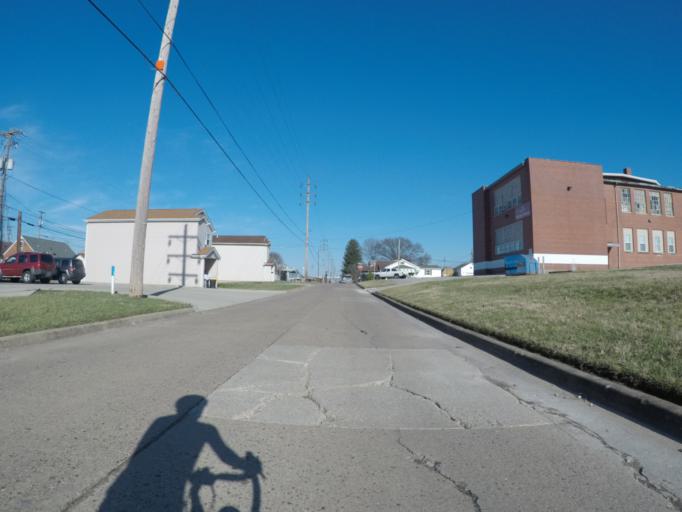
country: US
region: West Virginia
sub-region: Cabell County
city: Huntington
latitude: 38.4087
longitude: -82.4879
